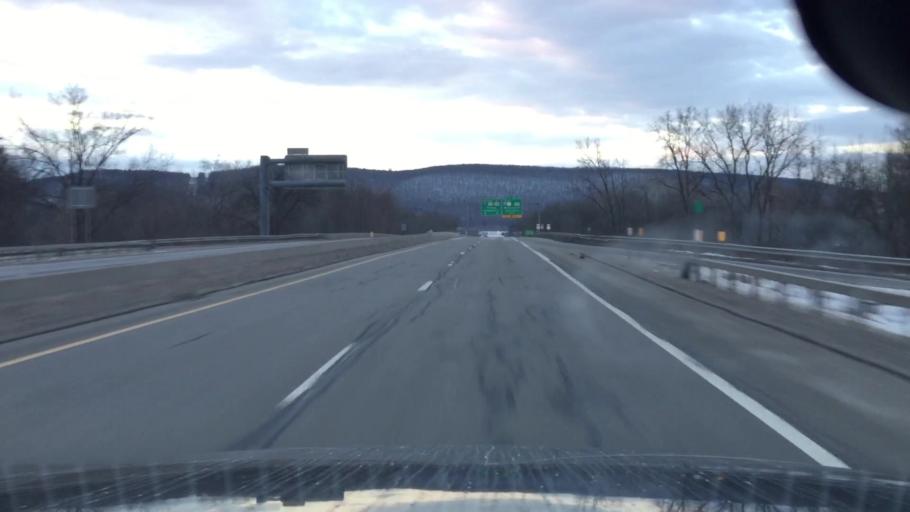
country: US
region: New York
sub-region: Steuben County
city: Painted Post
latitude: 42.1695
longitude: -77.1045
